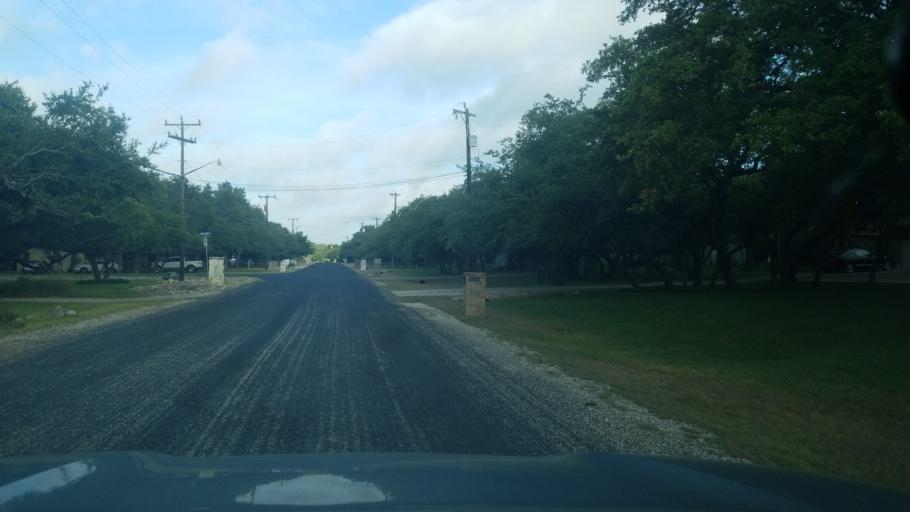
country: US
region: Texas
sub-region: Bexar County
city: Timberwood Park
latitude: 29.6991
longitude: -98.5022
